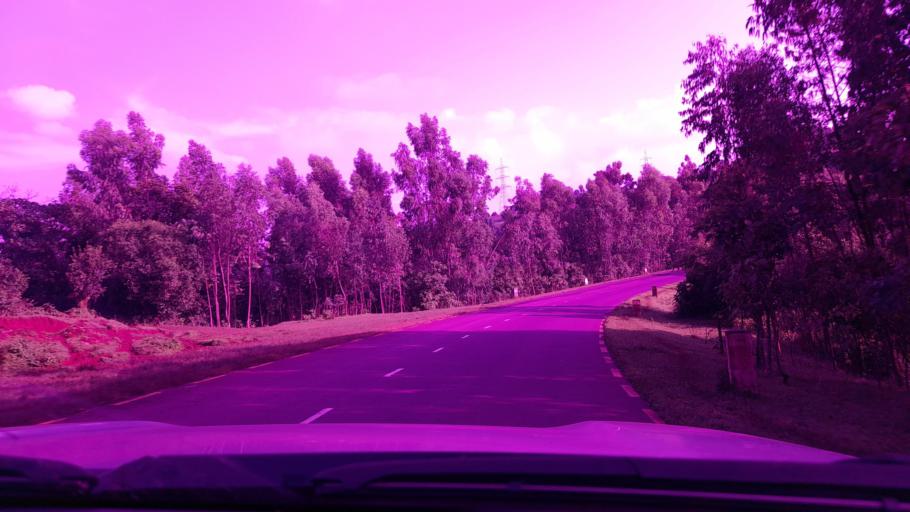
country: ET
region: Oromiya
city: Bedele
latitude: 8.1447
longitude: 36.4582
